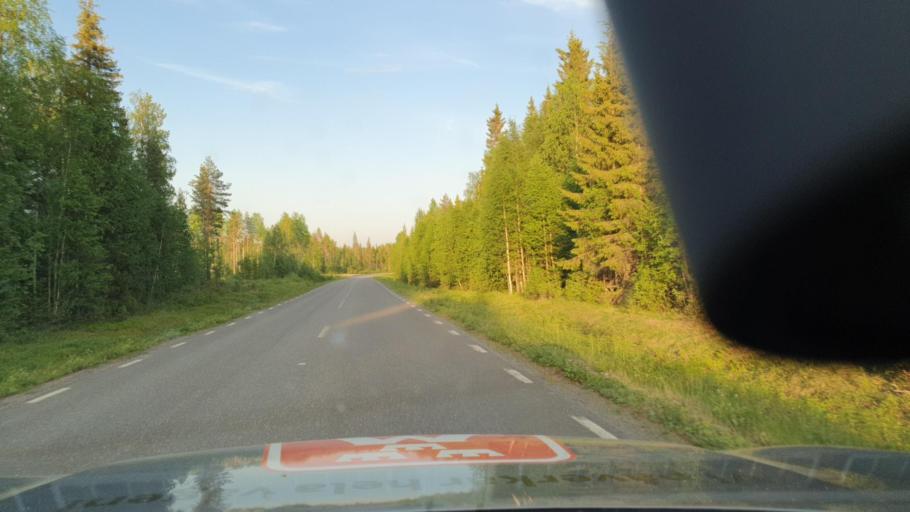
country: SE
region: Norrbotten
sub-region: Bodens Kommun
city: Boden
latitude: 66.2103
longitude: 21.4473
